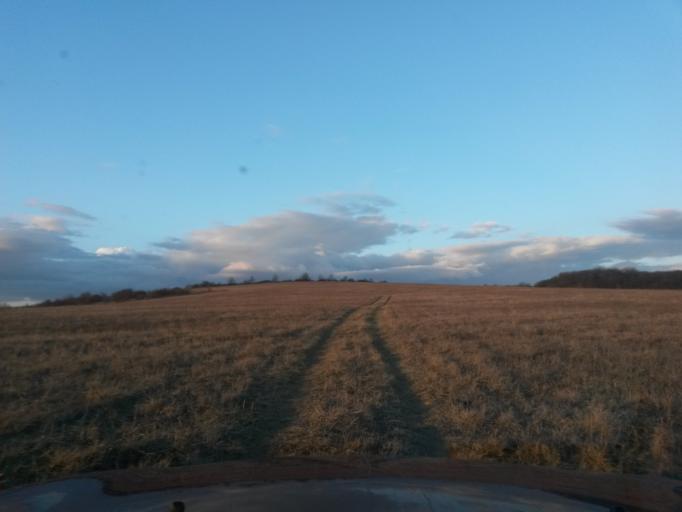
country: SK
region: Kosicky
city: Kosice
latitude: 48.6986
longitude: 21.3505
